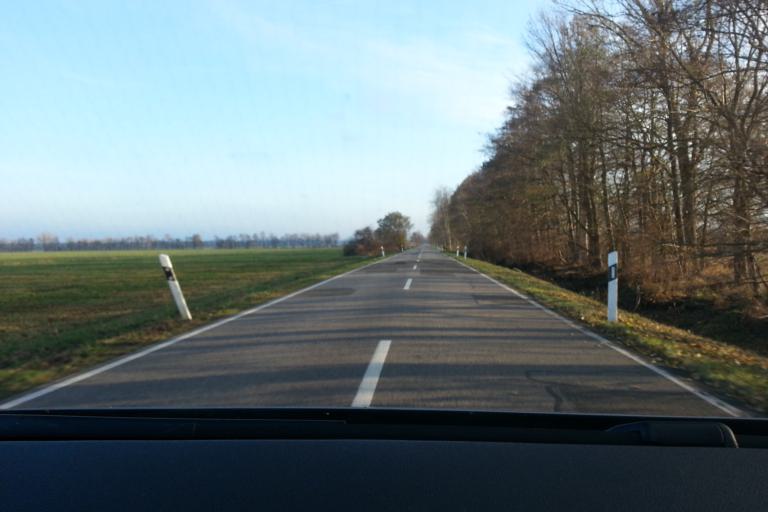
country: DE
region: Mecklenburg-Vorpommern
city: Strasburg
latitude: 53.6396
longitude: 13.7456
